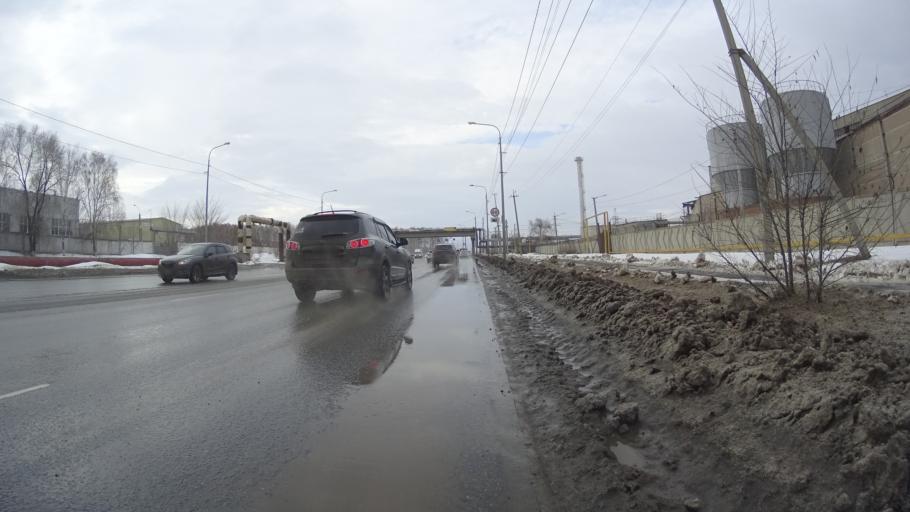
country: RU
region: Chelyabinsk
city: Roshchino
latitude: 55.2069
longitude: 61.3198
